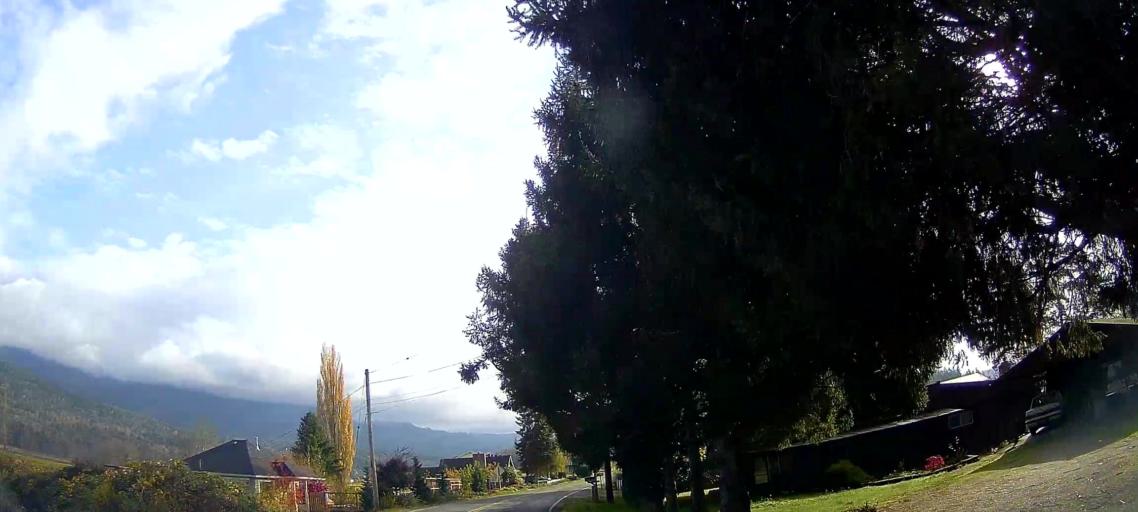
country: US
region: Washington
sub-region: Skagit County
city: Clear Lake
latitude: 48.4561
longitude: -122.2346
